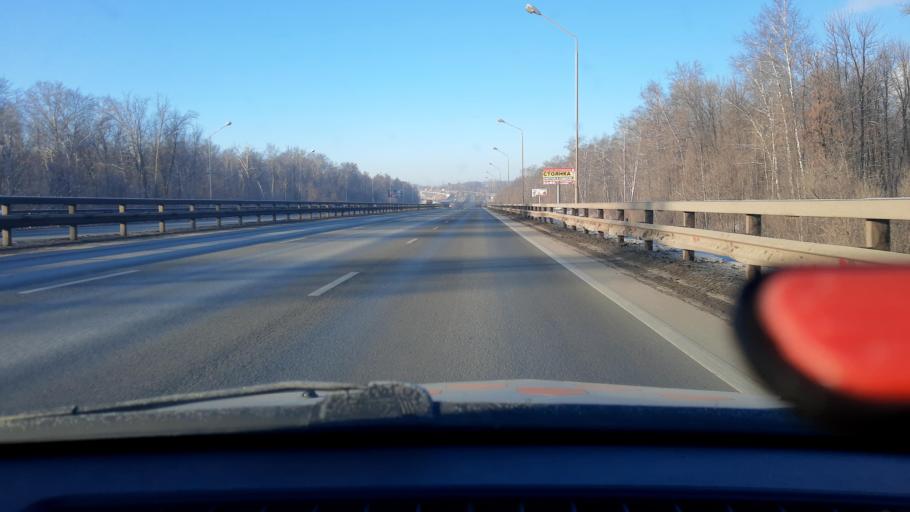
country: RU
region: Bashkortostan
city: Avdon
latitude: 54.6733
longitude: 55.8275
